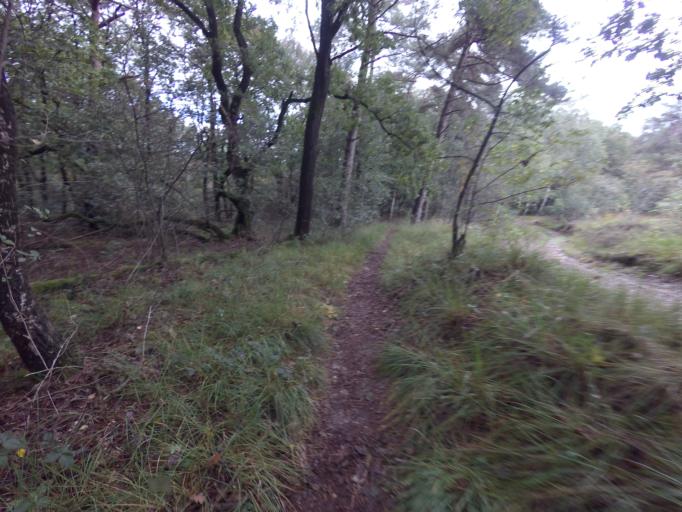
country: NL
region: Utrecht
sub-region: Gemeente Soest
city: Soest
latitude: 52.1338
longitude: 5.2985
